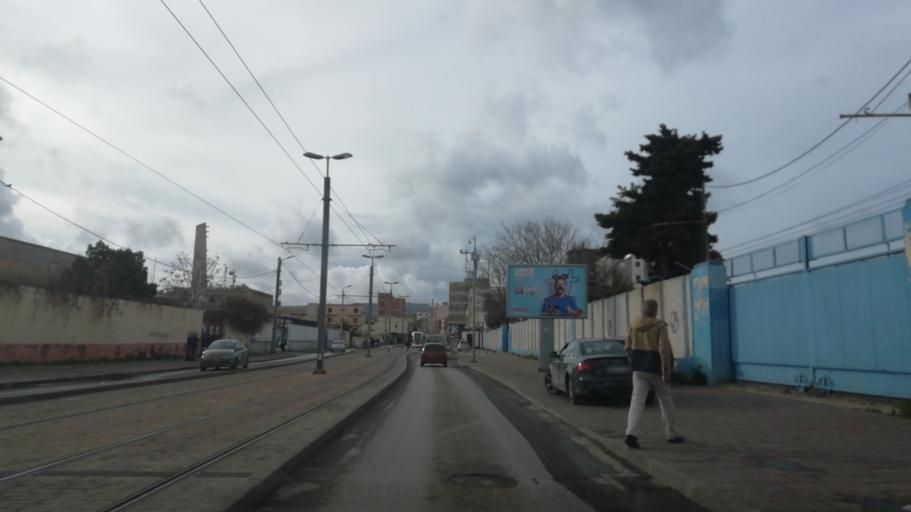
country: DZ
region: Oran
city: Oran
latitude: 35.6977
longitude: -0.6162
